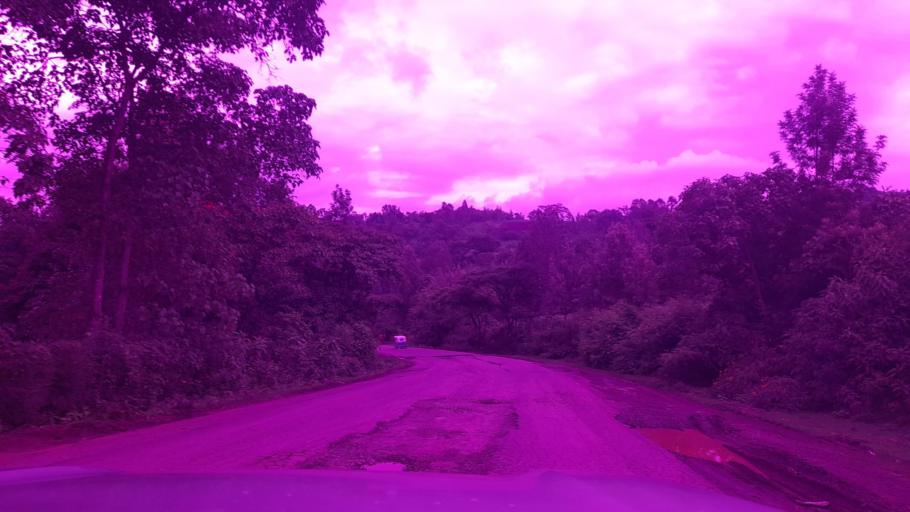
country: ET
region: Oromiya
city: Jima
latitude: 7.9196
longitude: 37.4064
